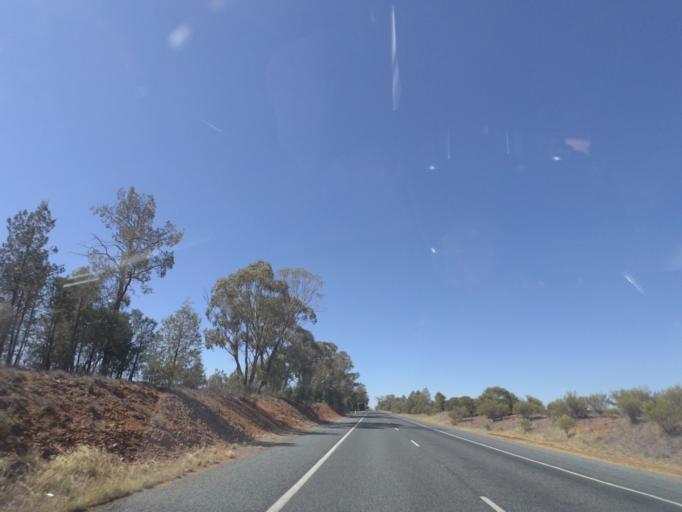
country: AU
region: New South Wales
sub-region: Bland
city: West Wyalong
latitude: -34.1622
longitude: 147.1165
